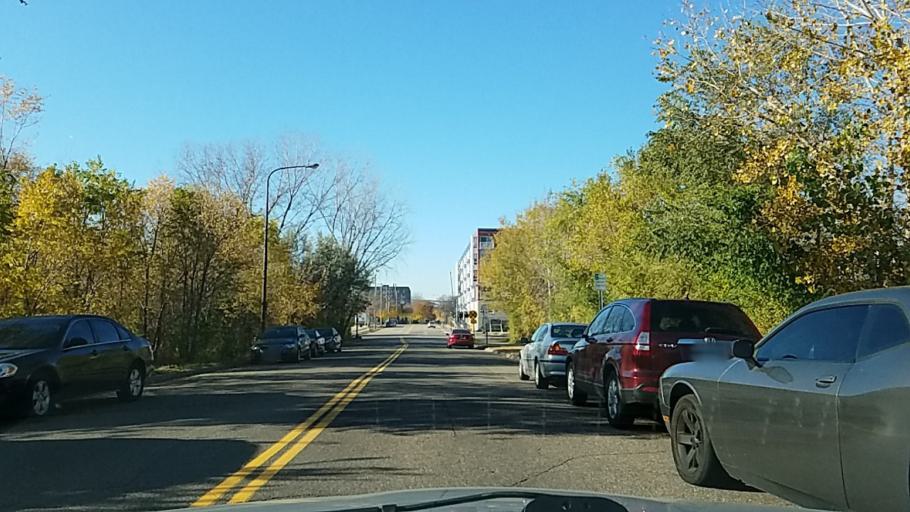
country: US
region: Minnesota
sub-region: Ramsey County
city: Saint Paul
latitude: 44.9406
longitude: -93.0869
